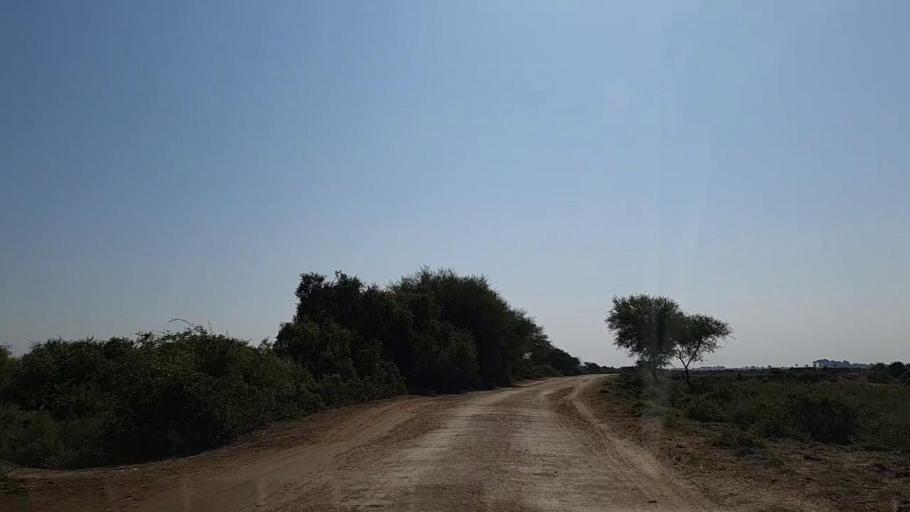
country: PK
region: Sindh
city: Chuhar Jamali
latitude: 24.5129
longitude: 68.0967
